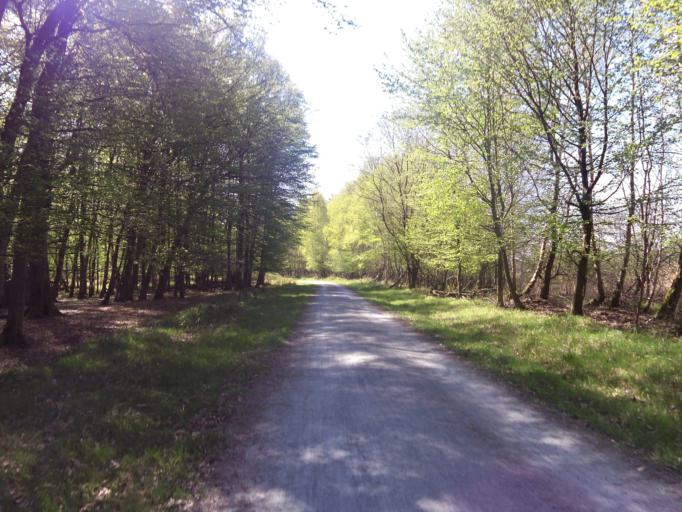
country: DE
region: Hesse
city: Morfelden-Walldorf
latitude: 49.9844
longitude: 8.5216
